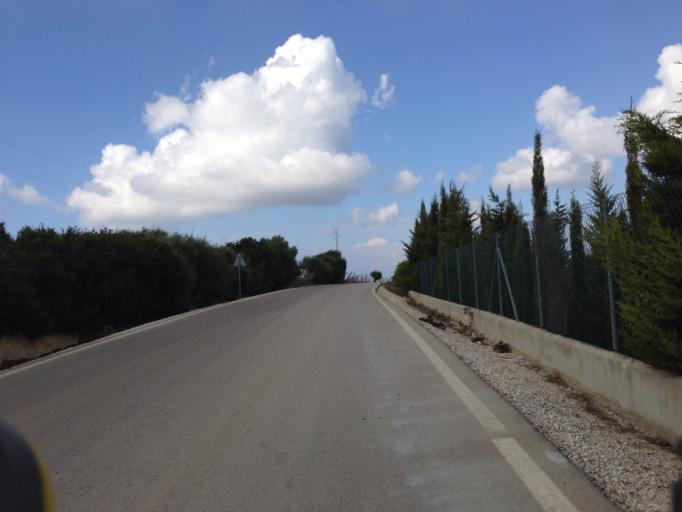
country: ES
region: Andalusia
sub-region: Provincia de Cadiz
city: Conil de la Frontera
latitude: 36.3458
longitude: -6.0490
